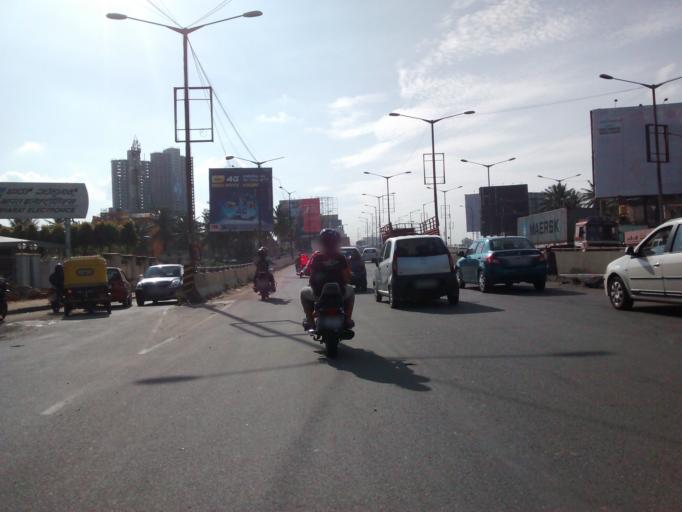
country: IN
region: Karnataka
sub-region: Bangalore Urban
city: Yelahanka
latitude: 13.0410
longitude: 77.6164
